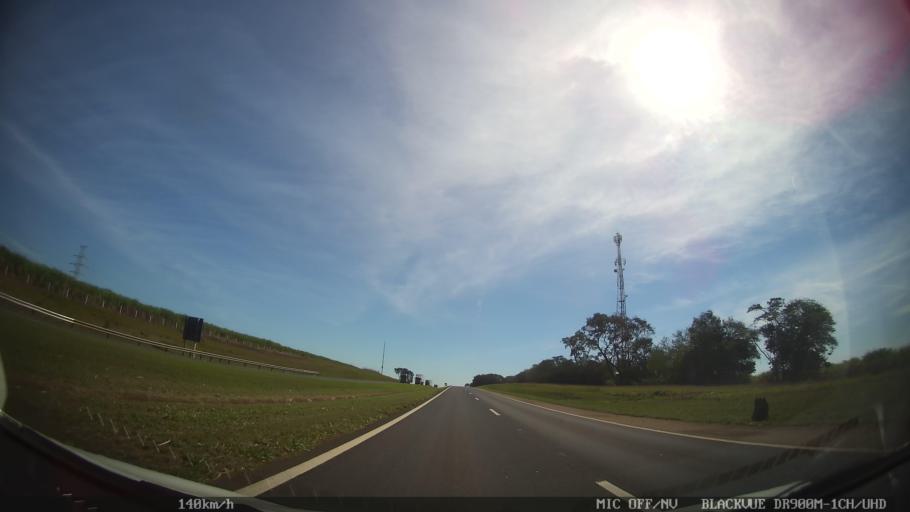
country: BR
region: Sao Paulo
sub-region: Porto Ferreira
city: Porto Ferreira
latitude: -21.9260
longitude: -47.4703
